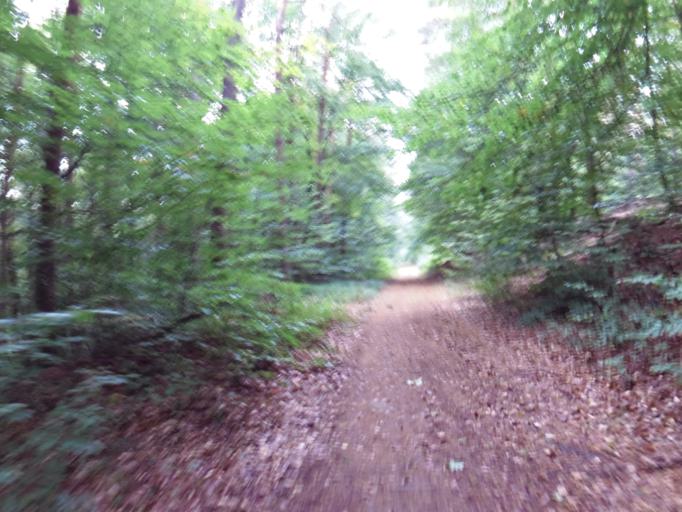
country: DE
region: Rheinland-Pfalz
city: Neuhemsbach
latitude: 49.5050
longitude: 7.9621
